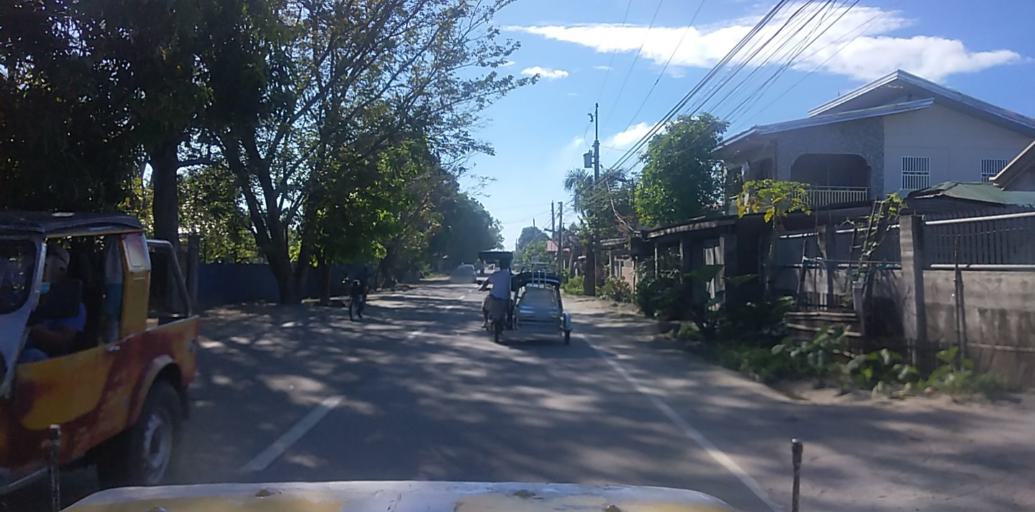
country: PH
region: Central Luzon
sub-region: Province of Pampanga
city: San Patricio
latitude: 15.0846
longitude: 120.7154
